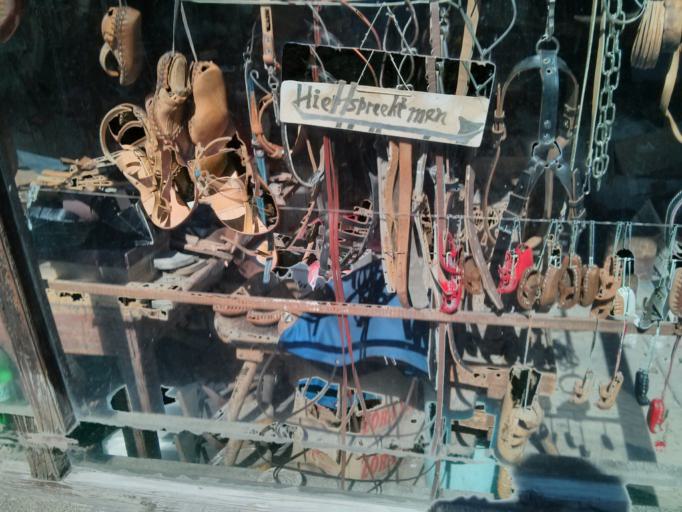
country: MK
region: Ohrid
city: Ohrid
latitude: 41.1165
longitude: 20.7996
